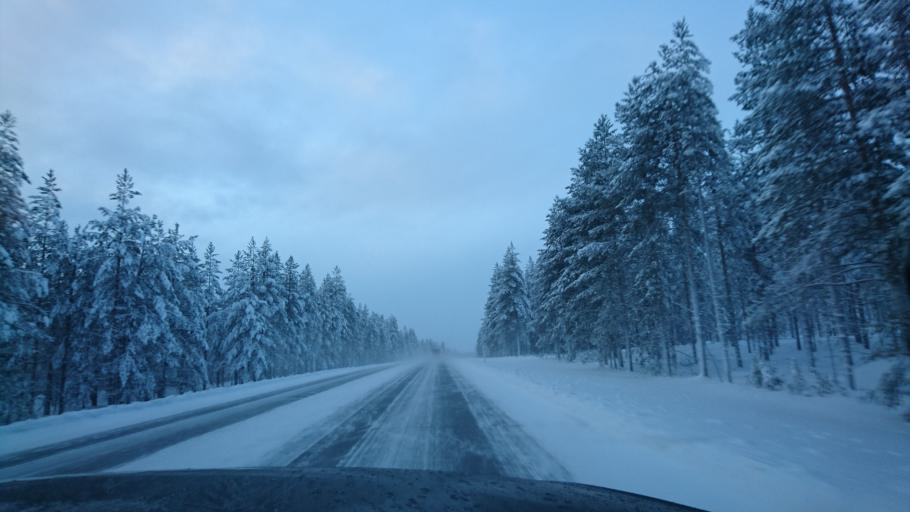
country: FI
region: Kainuu
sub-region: Kehys-Kainuu
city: Puolanka
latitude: 65.4379
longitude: 27.5982
